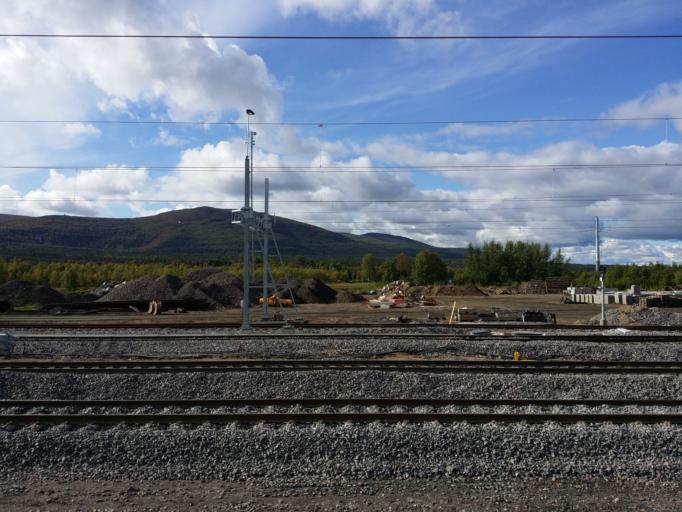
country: SE
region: Norrbotten
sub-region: Gallivare Kommun
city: Gaellivare
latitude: 67.1350
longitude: 20.6484
